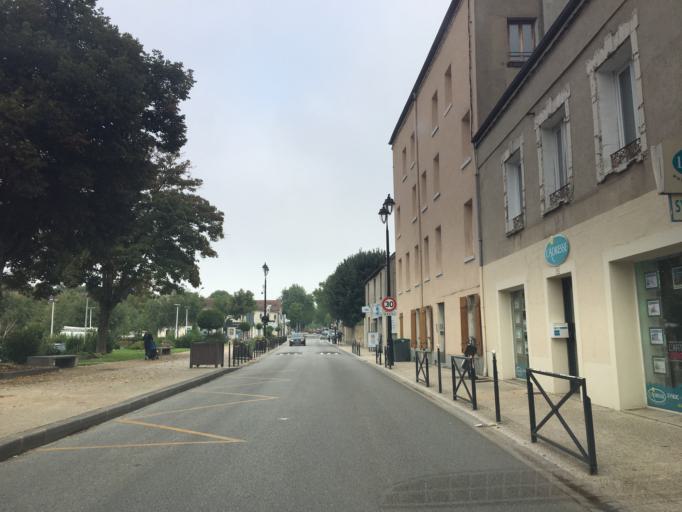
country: FR
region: Ile-de-France
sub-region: Departement de Seine-et-Marne
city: Brie-Comte-Robert
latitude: 48.6934
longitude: 2.6114
